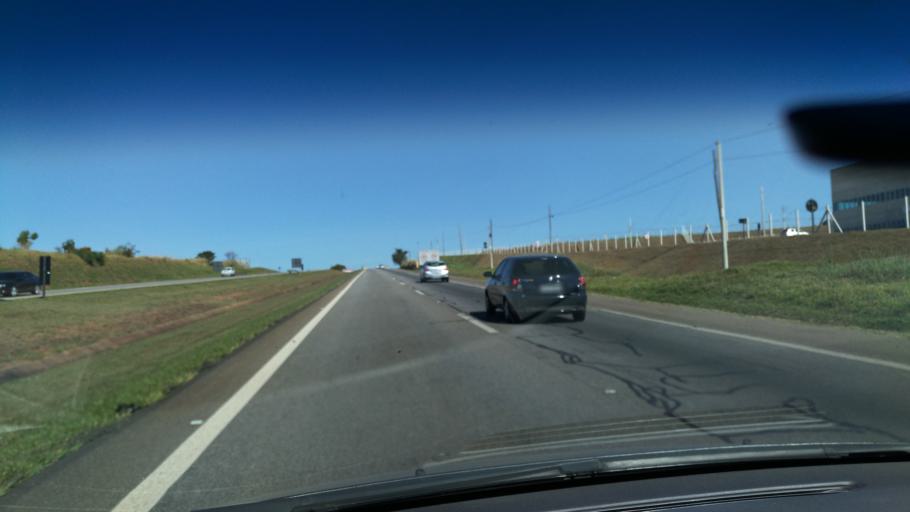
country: BR
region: Sao Paulo
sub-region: Santo Antonio De Posse
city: Santo Antonio de Posse
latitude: -22.5425
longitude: -46.9976
